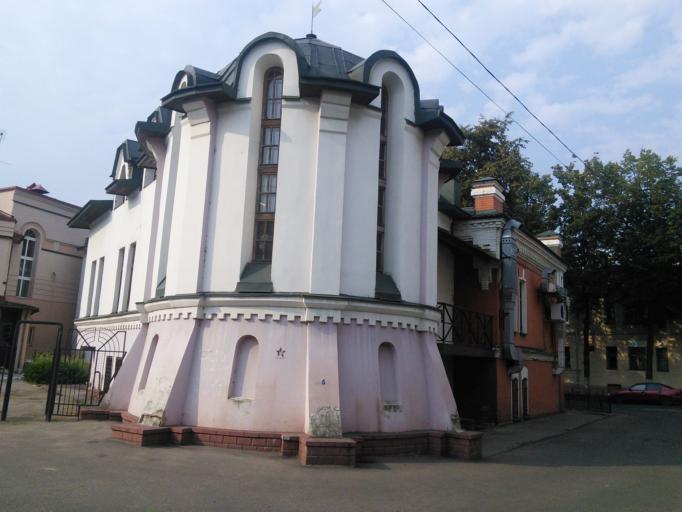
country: RU
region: Jaroslavl
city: Yaroslavl
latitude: 57.6225
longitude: 39.8779
